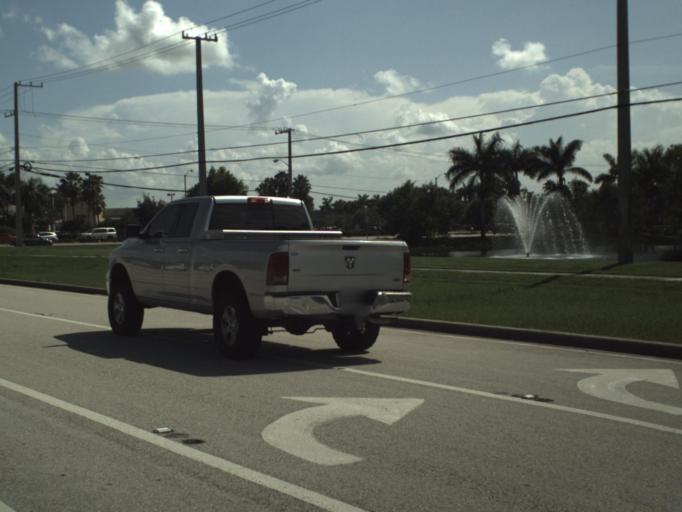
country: US
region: Florida
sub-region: Palm Beach County
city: Wellington
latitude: 26.6517
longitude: -80.2036
